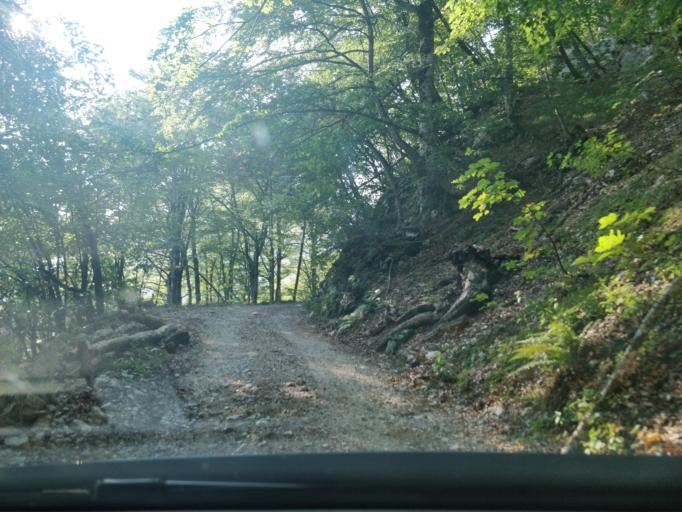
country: HR
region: Zadarska
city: Starigrad
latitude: 44.3803
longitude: 15.5420
